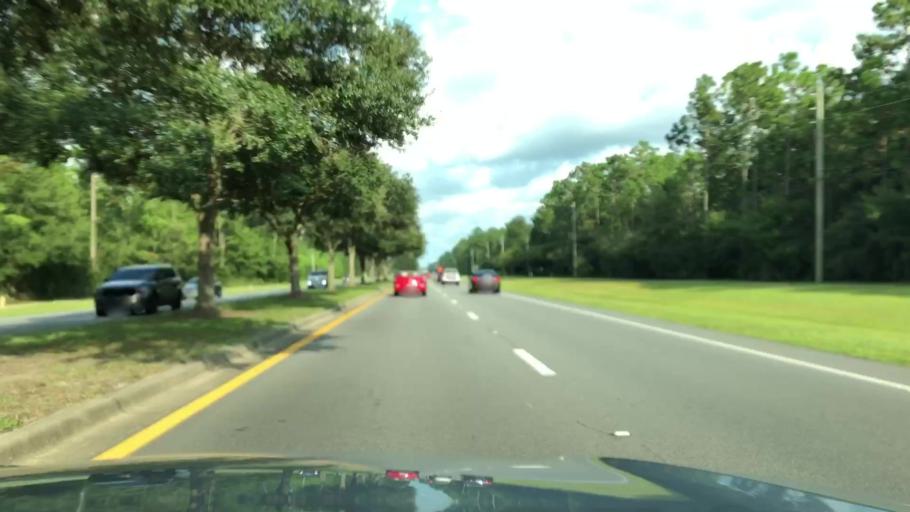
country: US
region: Florida
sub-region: Saint Johns County
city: Fruit Cove
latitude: 30.1103
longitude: -81.5709
